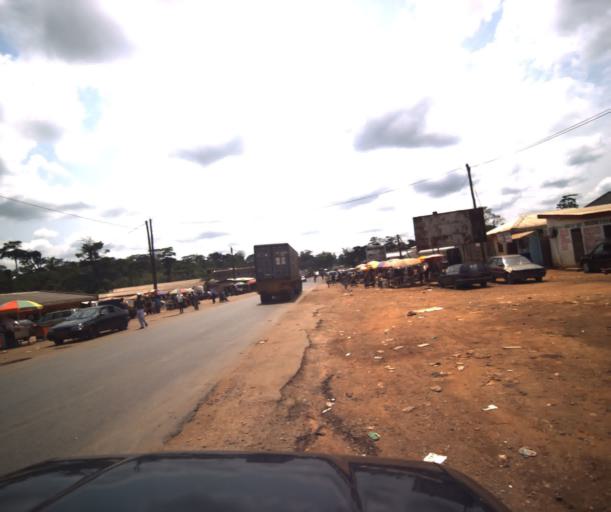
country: CM
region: Centre
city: Eseka
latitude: 3.8837
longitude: 10.8490
